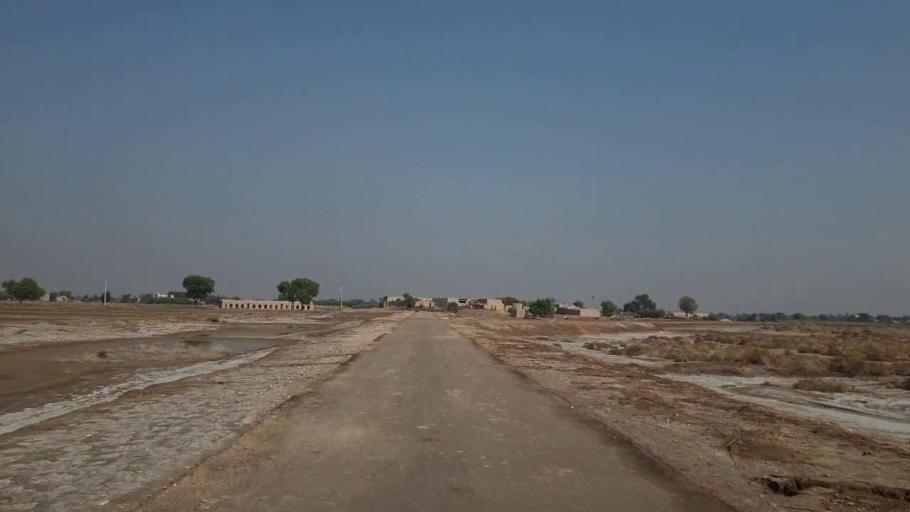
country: PK
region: Sindh
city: Sehwan
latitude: 26.4312
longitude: 67.7720
